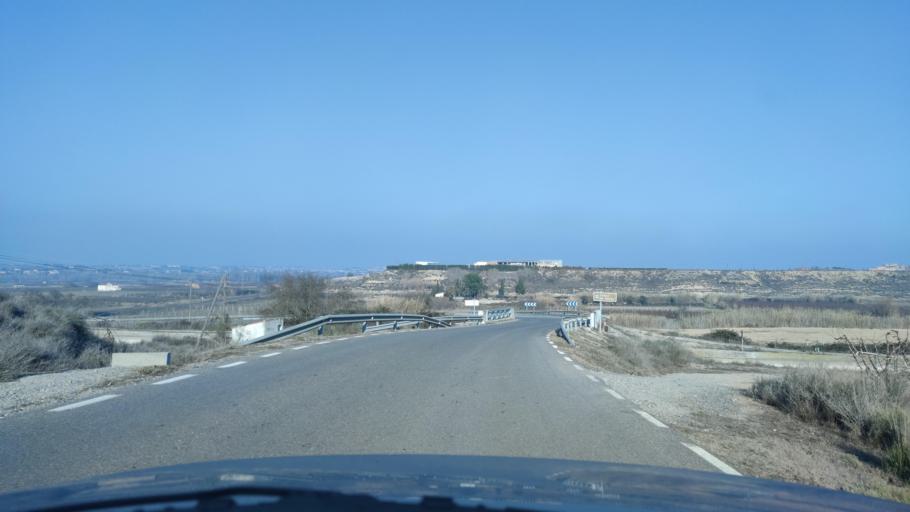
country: ES
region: Catalonia
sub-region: Provincia de Lleida
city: Sunyer
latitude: 41.5559
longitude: 0.5729
